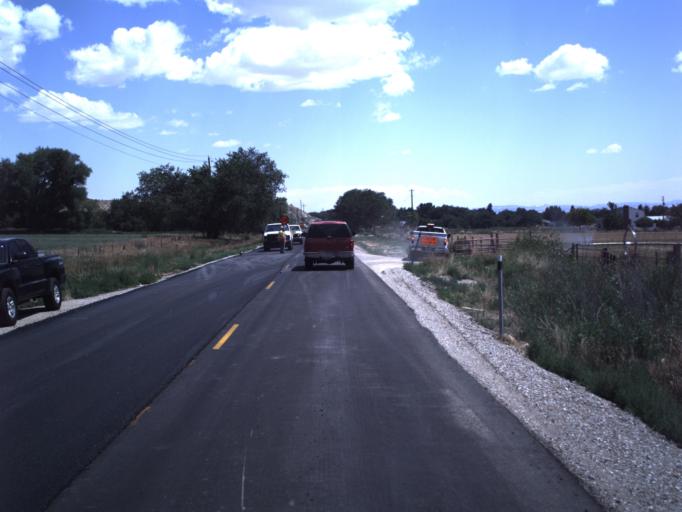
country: US
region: Utah
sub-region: Emery County
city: Orangeville
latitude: 39.2411
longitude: -111.0610
